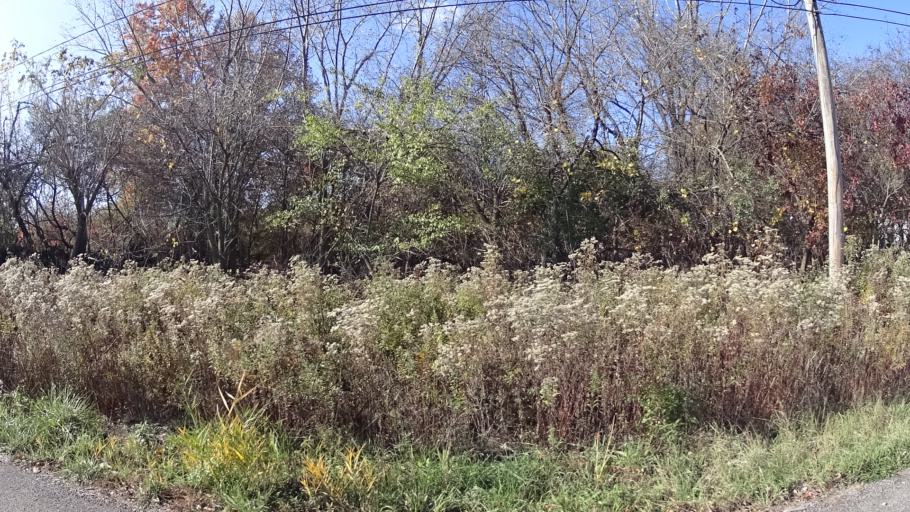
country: US
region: Ohio
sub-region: Lorain County
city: Lorain
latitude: 41.4638
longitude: -82.1613
